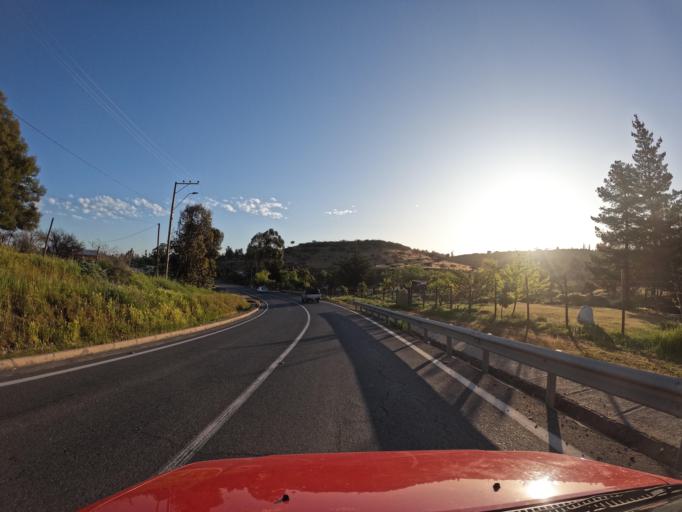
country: CL
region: O'Higgins
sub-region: Provincia de Colchagua
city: Santa Cruz
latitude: -34.2636
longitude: -71.7327
